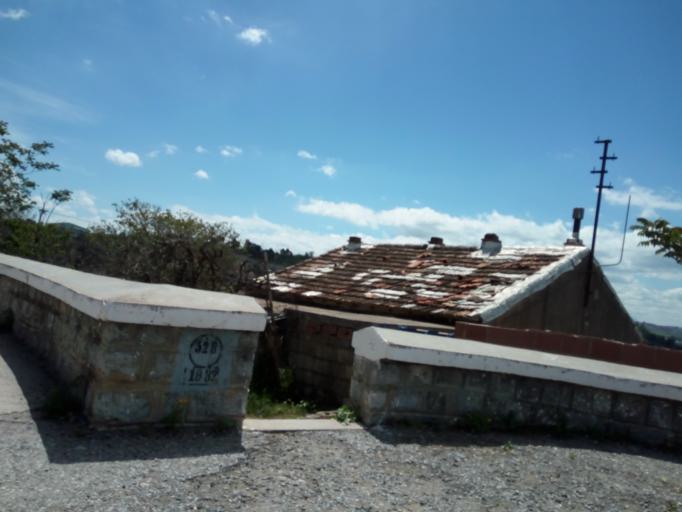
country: DZ
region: Constantine
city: Constantine
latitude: 36.3716
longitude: 6.6167
